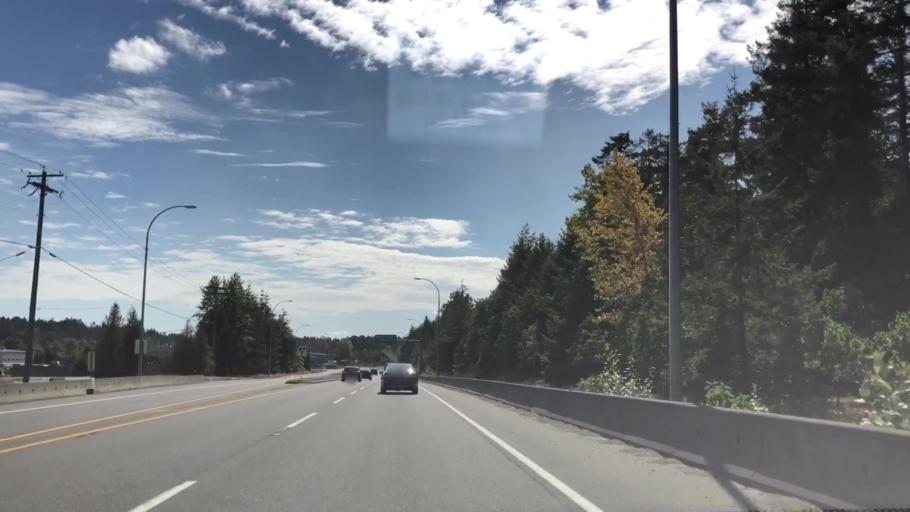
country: CA
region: British Columbia
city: Nanaimo
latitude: 49.1445
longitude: -123.8846
